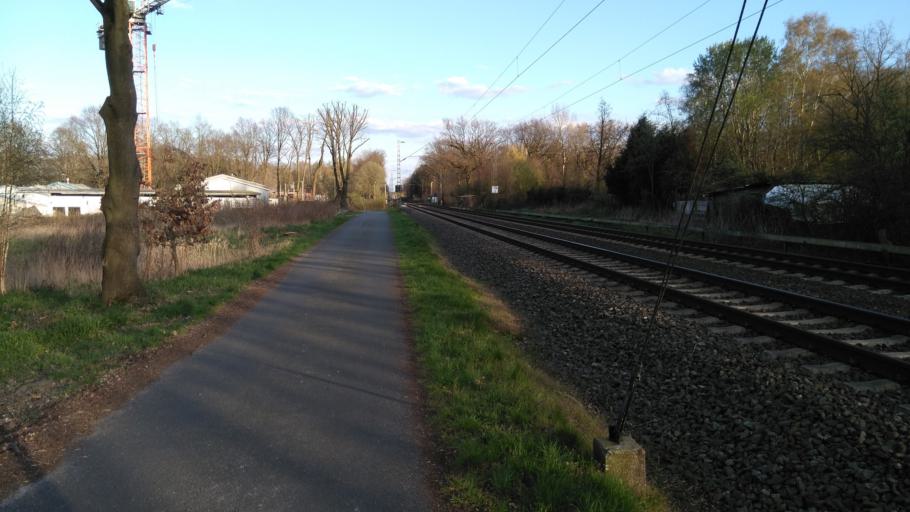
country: DE
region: Lower Saxony
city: Nottensdorf
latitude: 53.4941
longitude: 9.6077
